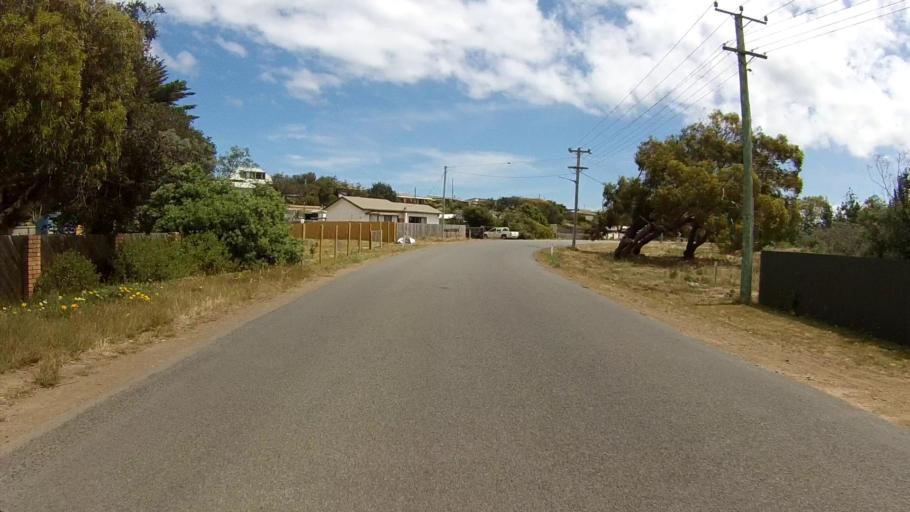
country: AU
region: Tasmania
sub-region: Sorell
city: Sorell
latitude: -42.8709
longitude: 147.6363
